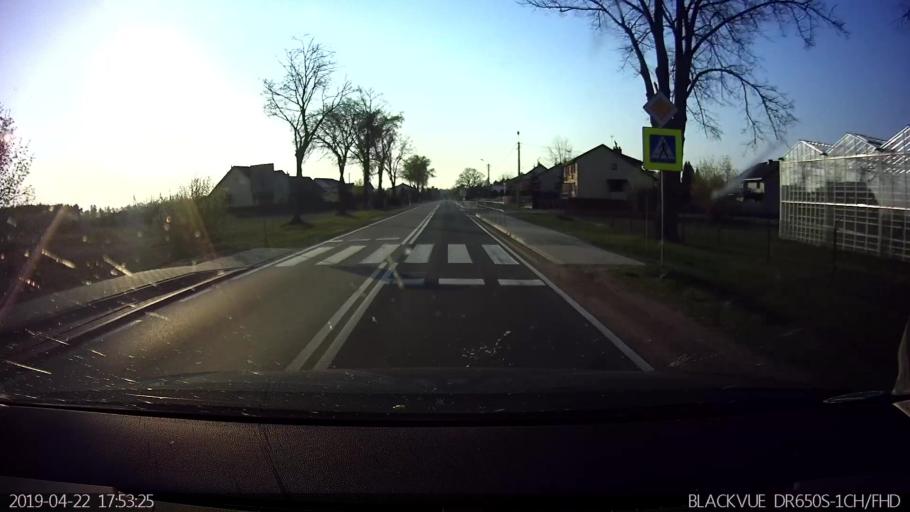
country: PL
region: Masovian Voivodeship
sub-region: Powiat wegrowski
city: Liw
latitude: 52.4528
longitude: 21.9549
